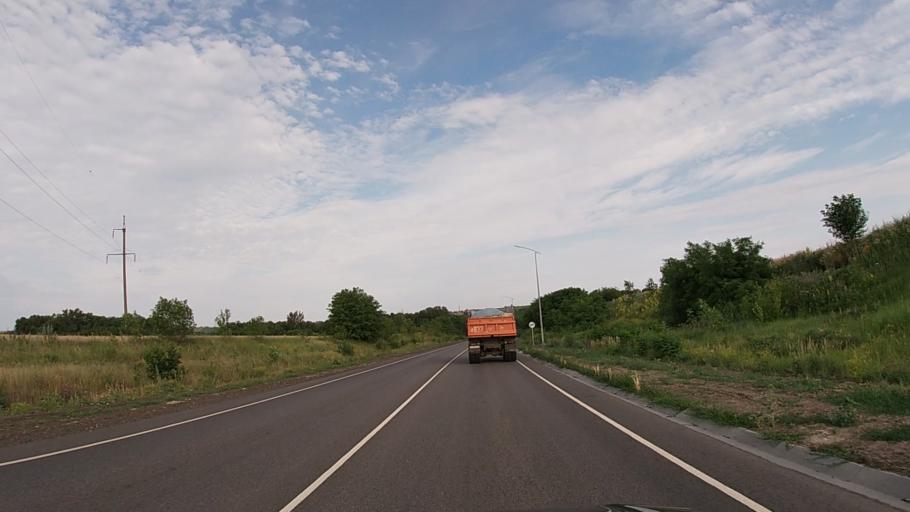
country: RU
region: Belgorod
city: Severnyy
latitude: 50.6664
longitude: 36.4958
